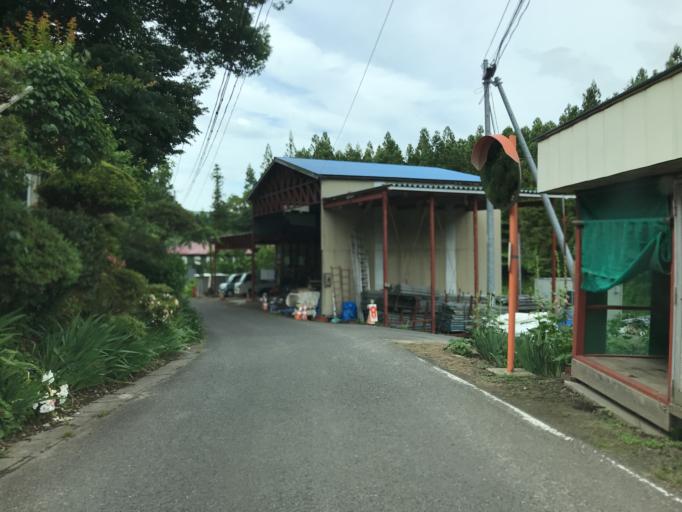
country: JP
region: Fukushima
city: Funehikimachi-funehiki
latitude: 37.5075
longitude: 140.6498
